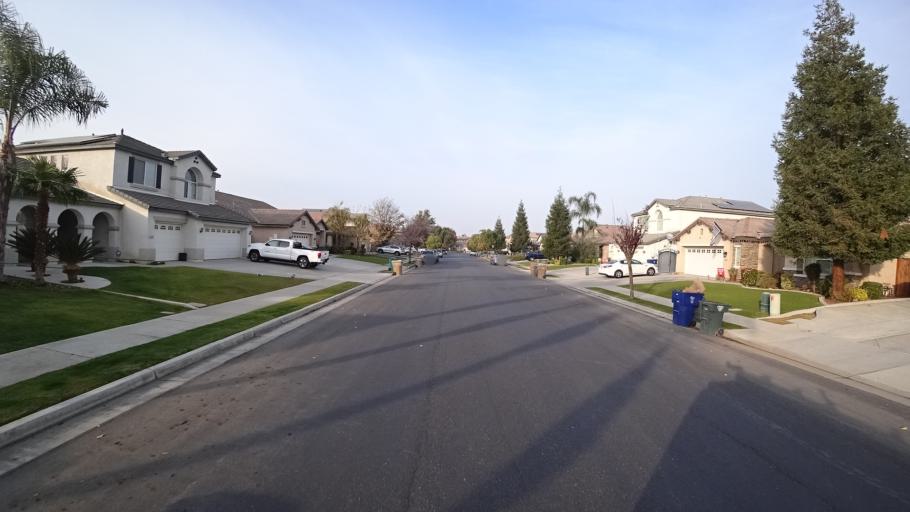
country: US
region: California
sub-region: Kern County
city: Greenacres
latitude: 35.4246
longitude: -119.1251
